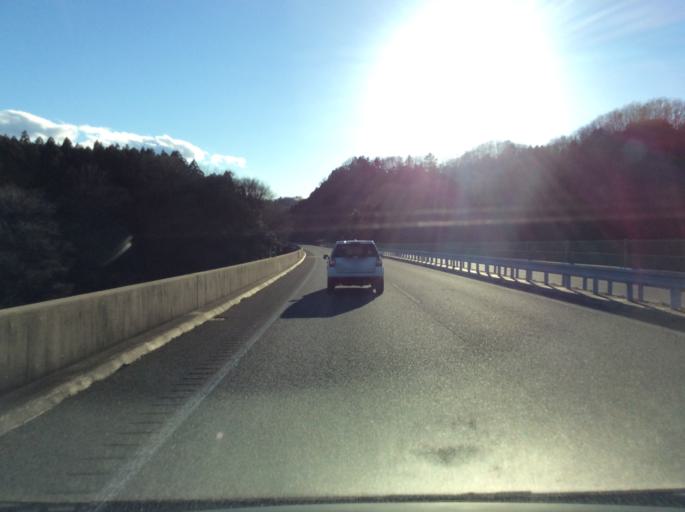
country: JP
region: Fukushima
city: Iwaki
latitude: 36.9837
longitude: 140.7985
